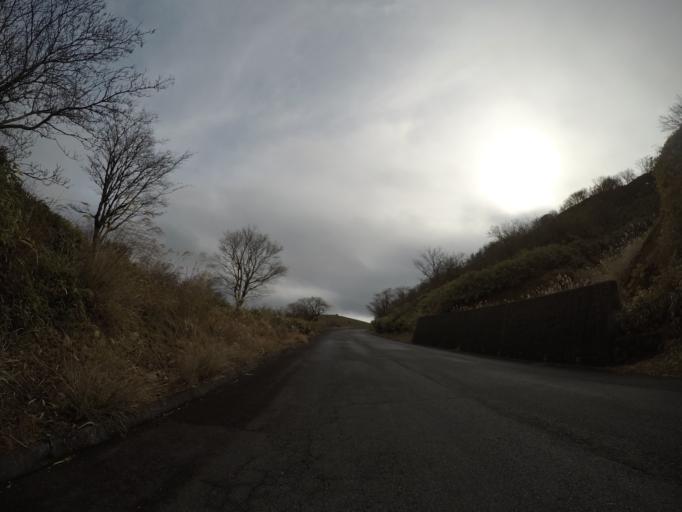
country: JP
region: Shizuoka
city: Heda
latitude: 34.8644
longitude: 138.8424
